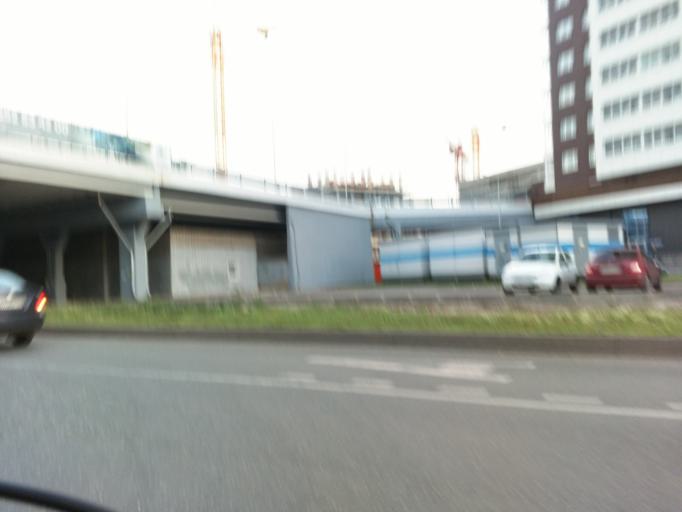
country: RU
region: Tatarstan
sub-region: Tukayevskiy Rayon
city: Naberezhnyye Chelny
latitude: 55.7525
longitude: 52.4117
